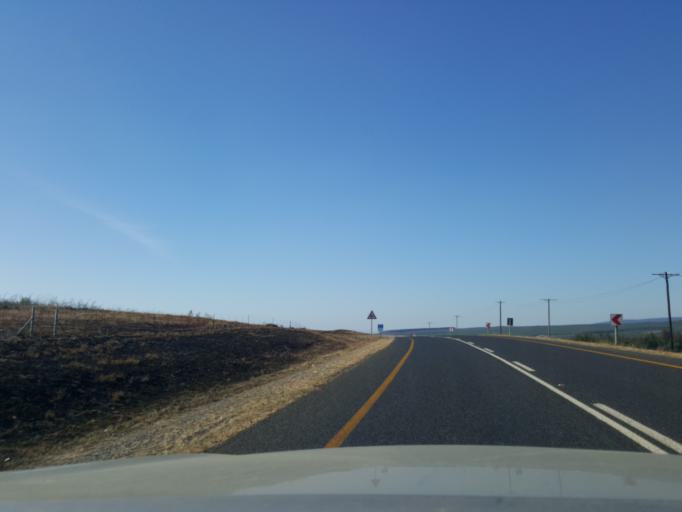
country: ZA
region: Mpumalanga
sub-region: Nkangala District Municipality
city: Belfast
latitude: -25.5322
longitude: 30.3392
